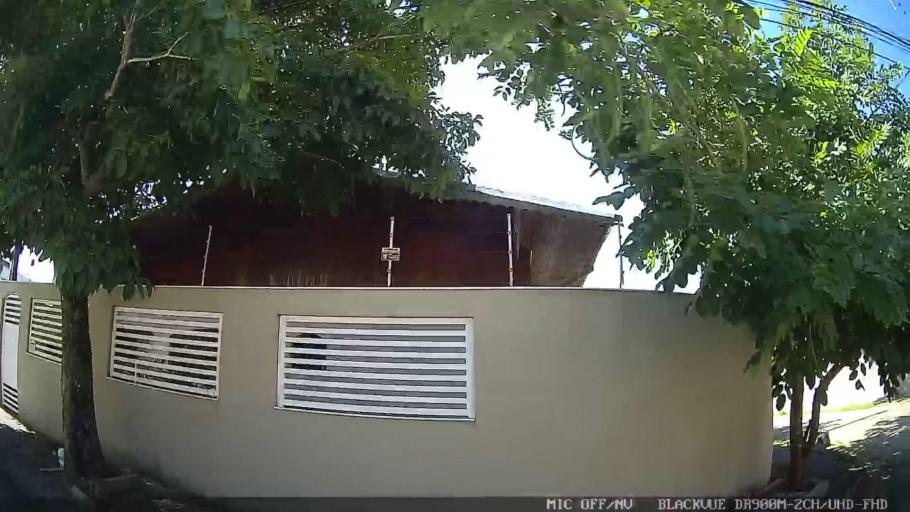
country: BR
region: Sao Paulo
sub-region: Peruibe
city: Peruibe
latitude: -24.3212
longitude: -46.9948
